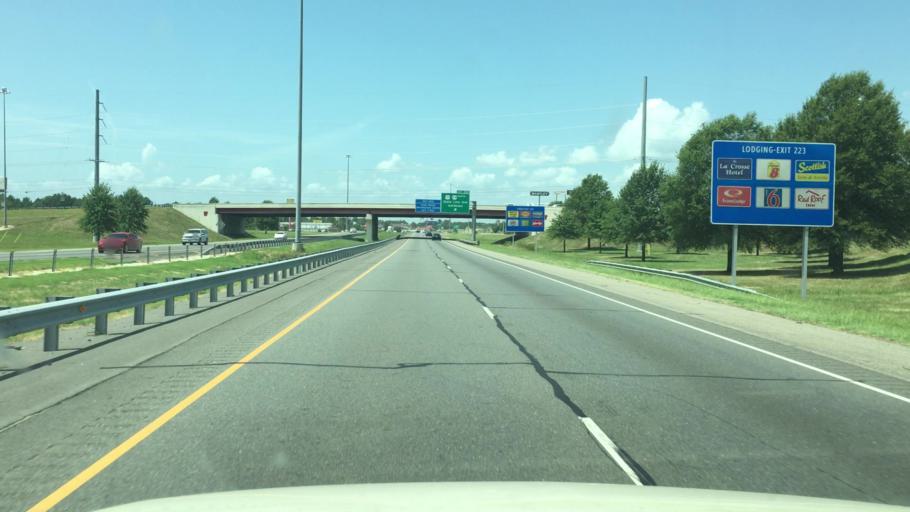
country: US
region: Arkansas
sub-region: Miller County
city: Texarkana
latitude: 33.4719
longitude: -94.0268
